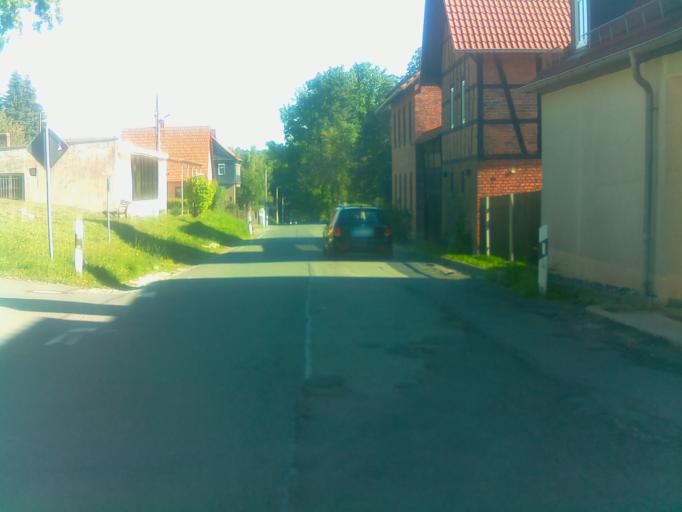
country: DE
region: Thuringia
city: Trockenborn-Wolfersdorf
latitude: 50.7879
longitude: 11.6957
